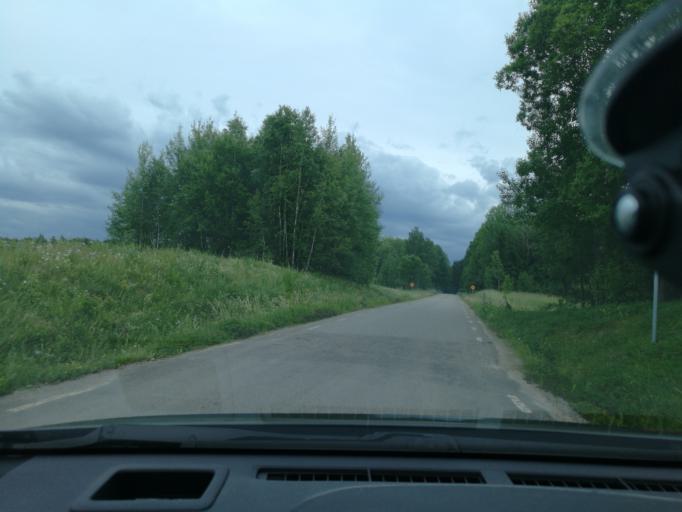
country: SE
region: Vaestmanland
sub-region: Surahammars Kommun
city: Ramnas
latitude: 59.8477
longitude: 16.3122
